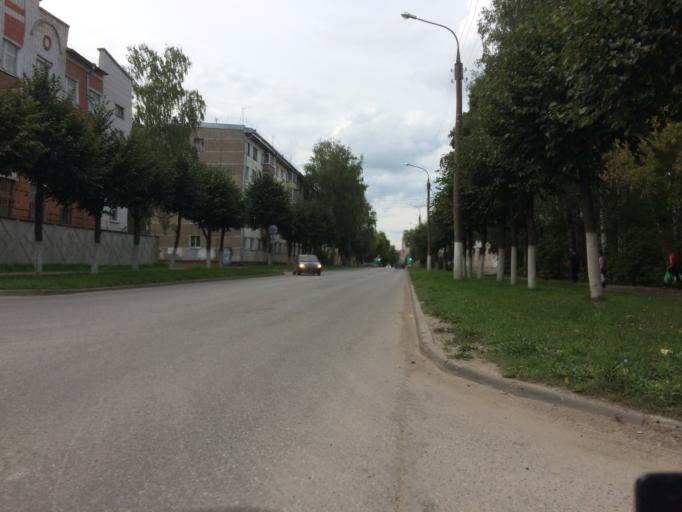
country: RU
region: Mariy-El
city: Yoshkar-Ola
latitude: 56.6341
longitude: 47.8728
